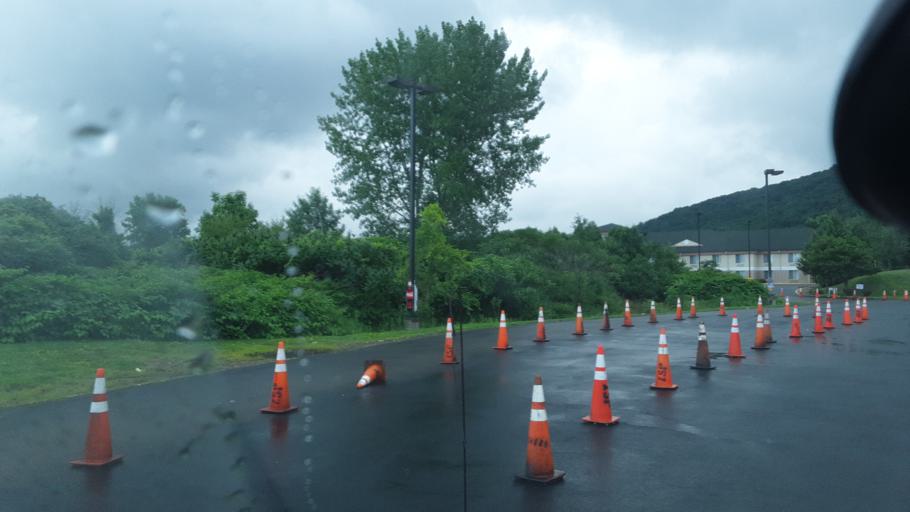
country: US
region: New York
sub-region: Cattaraugus County
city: Salamanca
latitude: 42.1581
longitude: -78.7479
